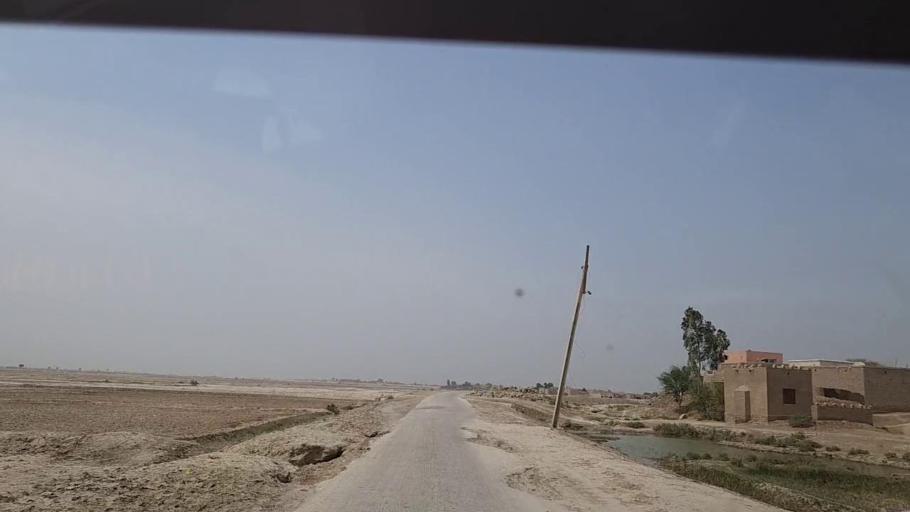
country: PK
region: Sindh
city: Khairpur Nathan Shah
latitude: 27.0635
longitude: 67.6484
